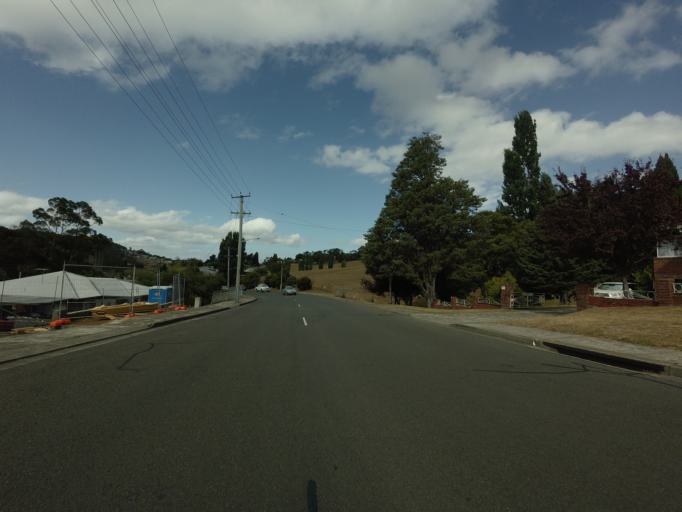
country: AU
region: Tasmania
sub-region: Hobart
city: Dynnyrne
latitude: -42.8979
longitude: 147.2897
